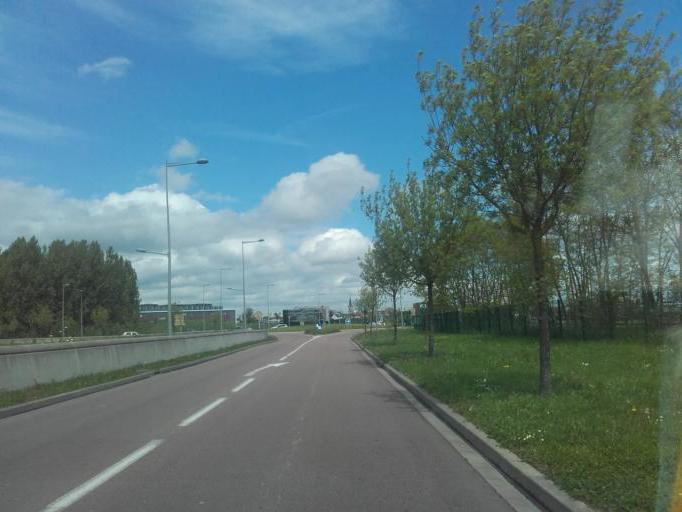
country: FR
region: Bourgogne
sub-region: Departement de Saone-et-Loire
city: Saint-Remy
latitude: 46.7723
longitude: 4.8403
